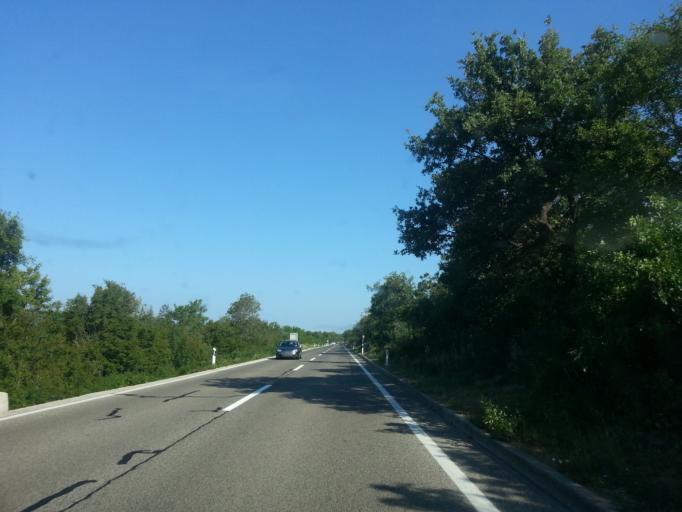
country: HR
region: Primorsko-Goranska
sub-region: Grad Crikvenica
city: Jadranovo
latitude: 45.2480
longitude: 14.6033
